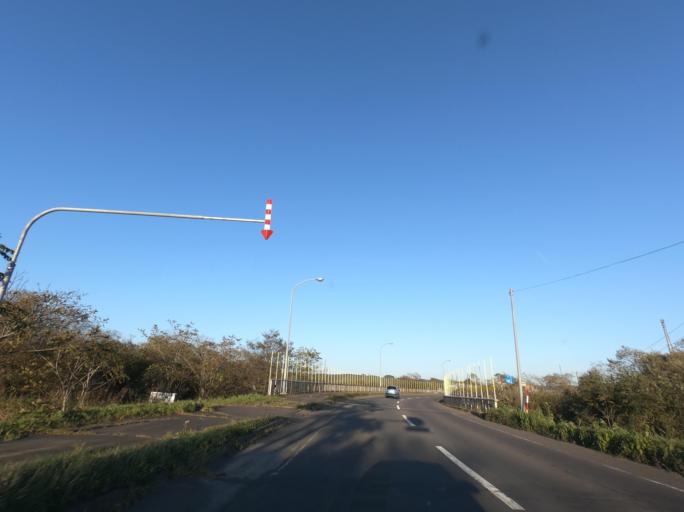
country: JP
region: Hokkaido
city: Kushiro
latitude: 43.0745
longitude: 144.2369
